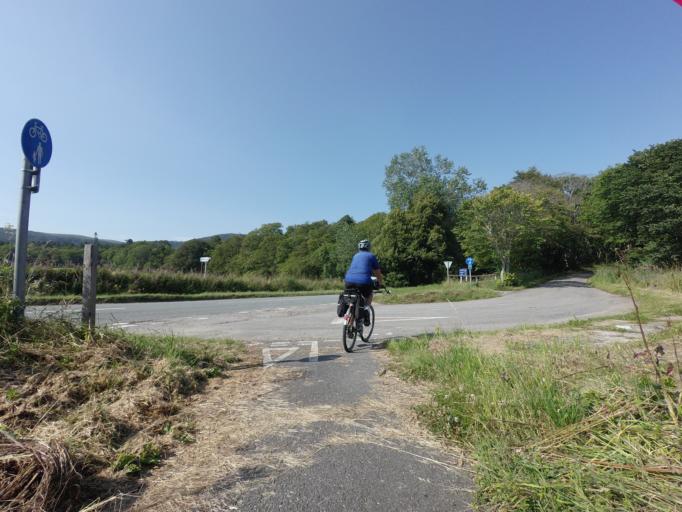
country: GB
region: Scotland
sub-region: Highland
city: Evanton
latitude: 57.6722
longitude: -4.3208
